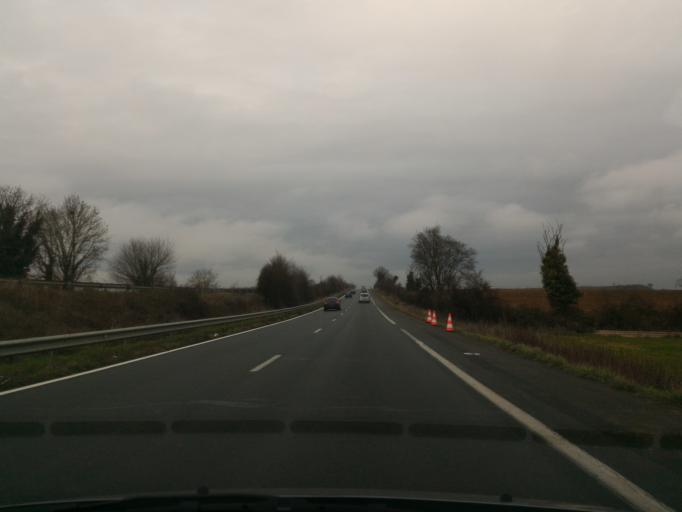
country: FR
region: Poitou-Charentes
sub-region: Departement de la Vienne
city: Vivonne
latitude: 46.4412
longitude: 0.2652
